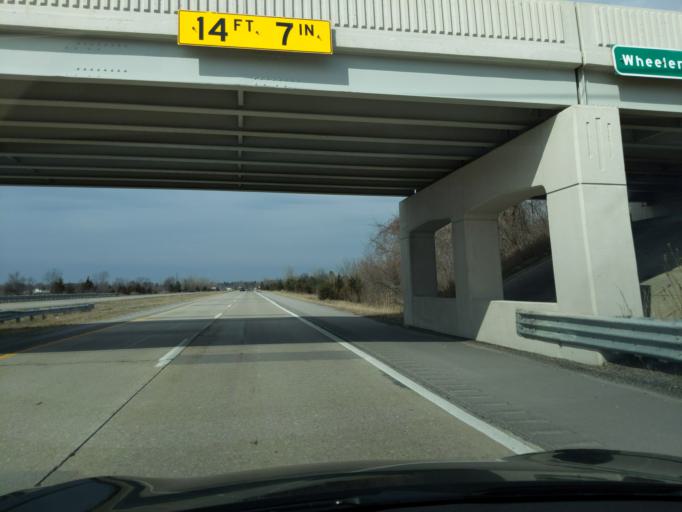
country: US
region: Michigan
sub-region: Bay County
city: Bay City
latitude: 43.6384
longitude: -83.9415
